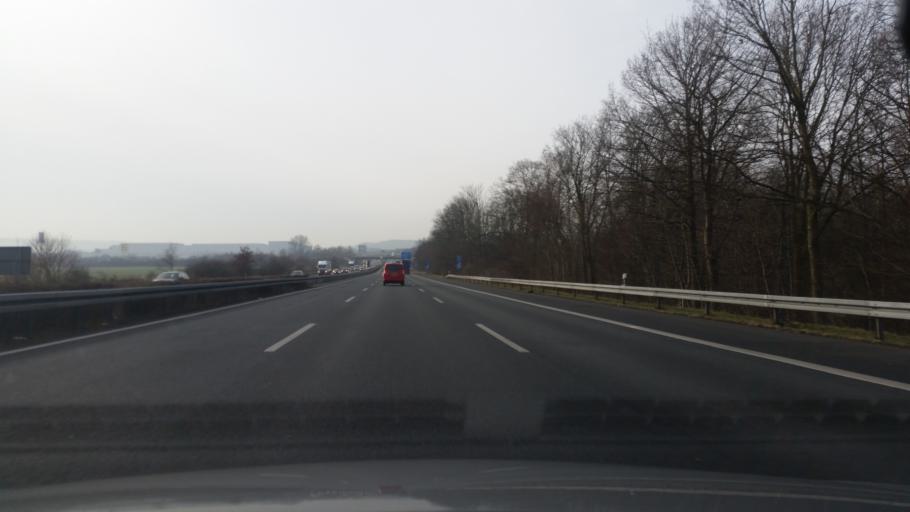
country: DE
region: Lower Saxony
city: Apelern
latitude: 52.2864
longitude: 9.3543
